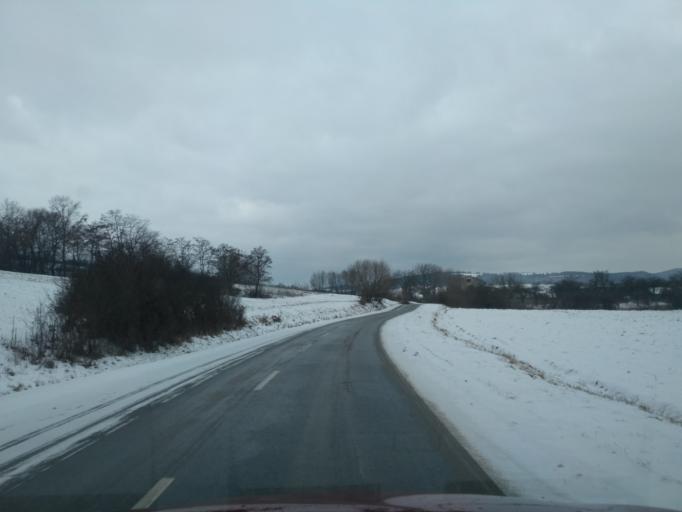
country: SK
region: Presovsky
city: Sabinov
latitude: 49.0525
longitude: 21.0806
